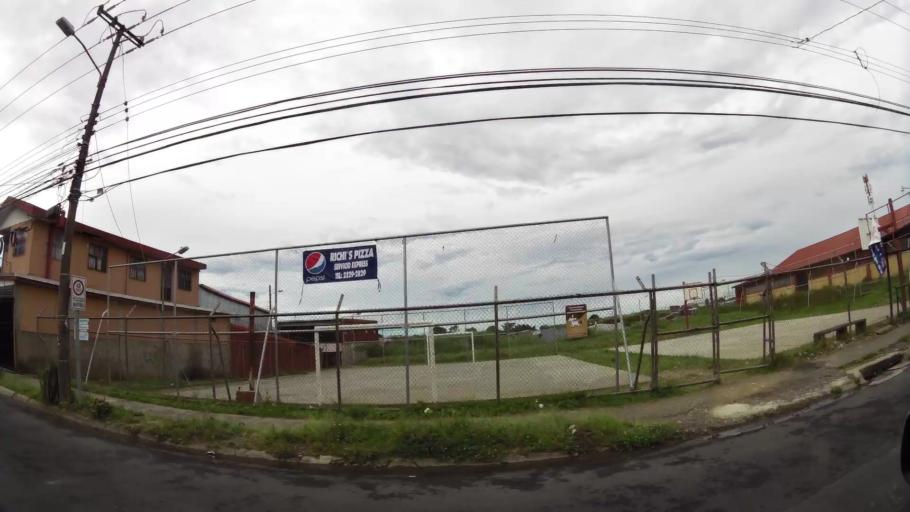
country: CR
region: San Jose
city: Purral
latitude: 9.9648
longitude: -84.0232
